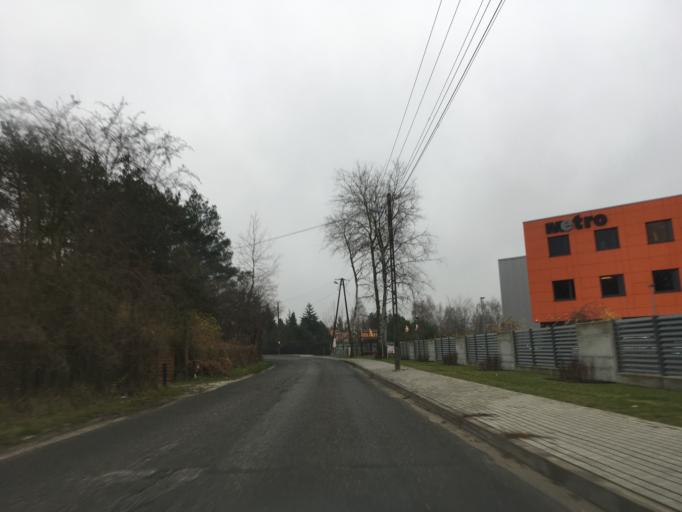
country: PL
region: Masovian Voivodeship
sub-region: Powiat piaseczynski
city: Lesznowola
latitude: 52.0722
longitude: 20.8778
